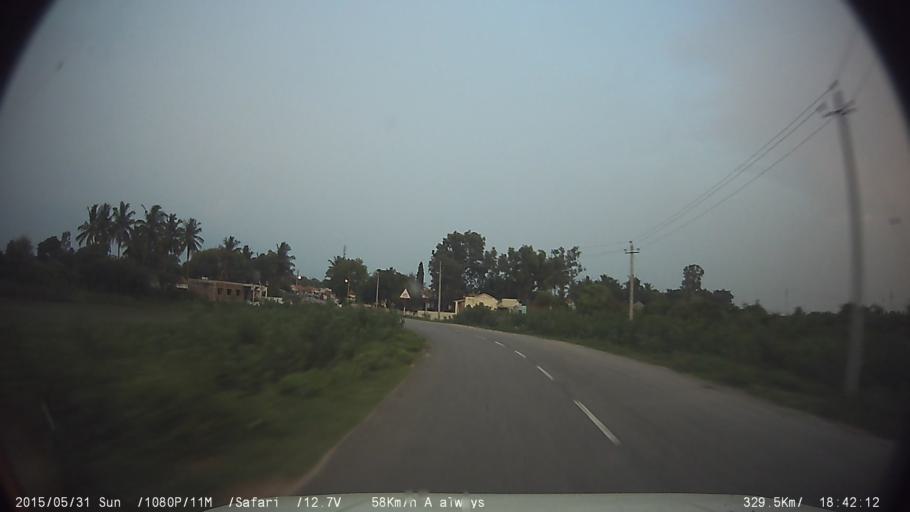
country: IN
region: Karnataka
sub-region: Mysore
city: Tirumakudal Narsipur
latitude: 12.1512
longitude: 76.7994
